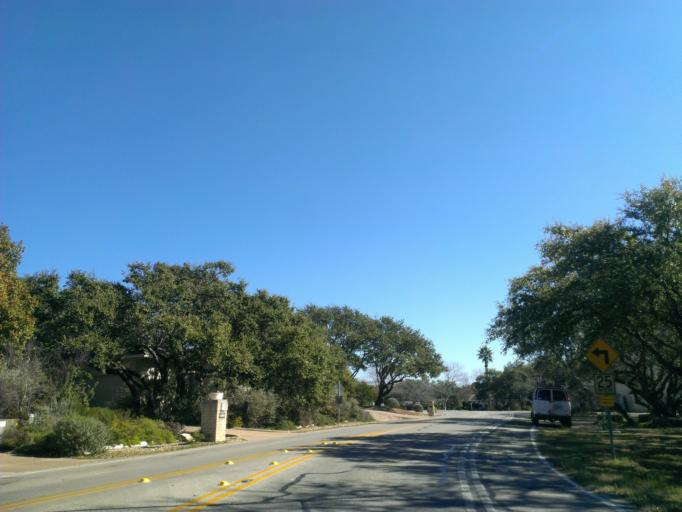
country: US
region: Texas
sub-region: Travis County
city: Lakeway
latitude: 30.3718
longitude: -97.9737
